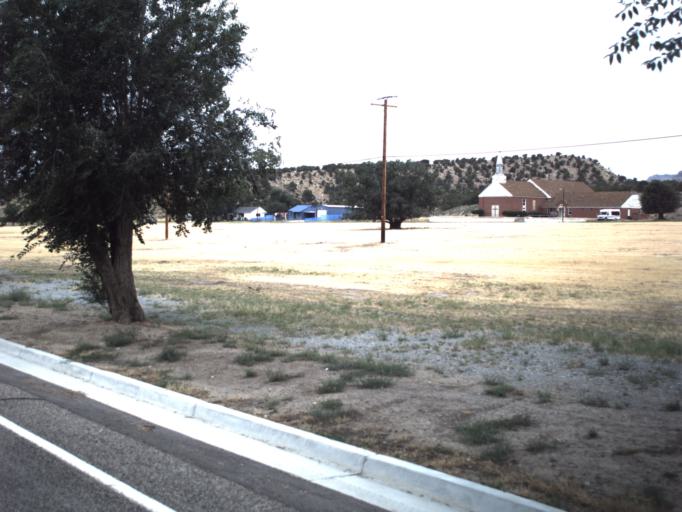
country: US
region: Utah
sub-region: Carbon County
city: East Carbon City
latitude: 39.5496
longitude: -110.3931
